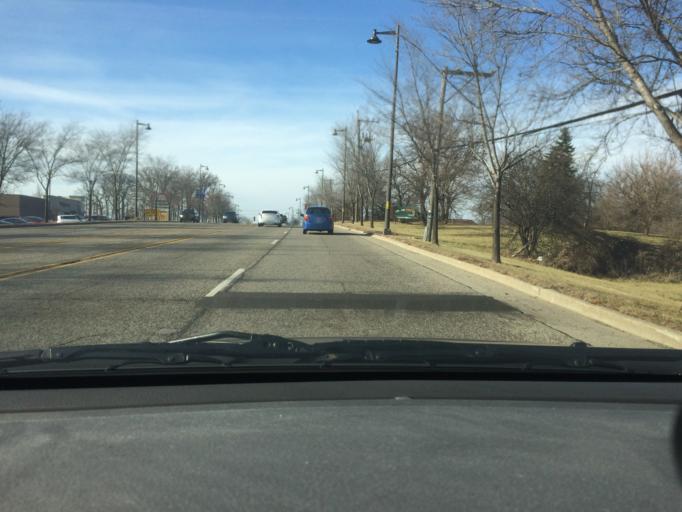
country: US
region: Illinois
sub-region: Cook County
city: Streamwood
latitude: 42.0130
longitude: -88.1798
